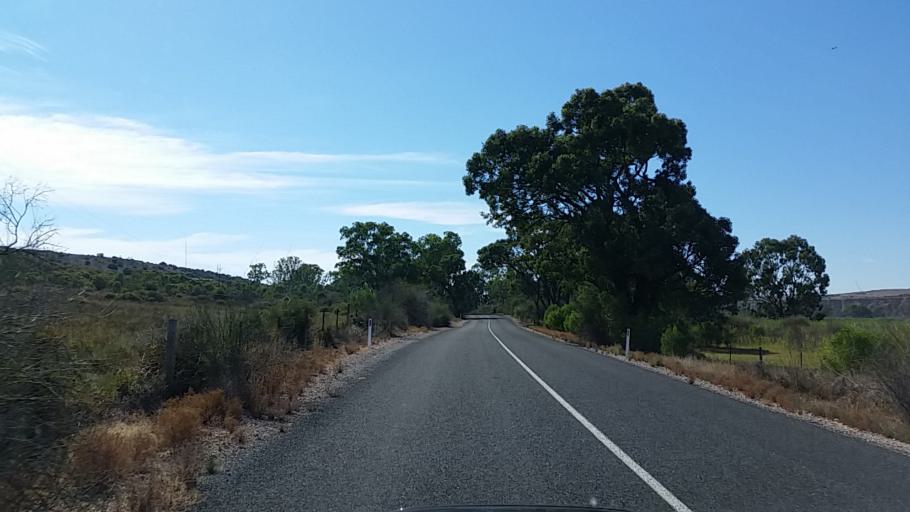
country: AU
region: South Australia
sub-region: Mid Murray
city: Mannum
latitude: -34.7199
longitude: 139.5495
